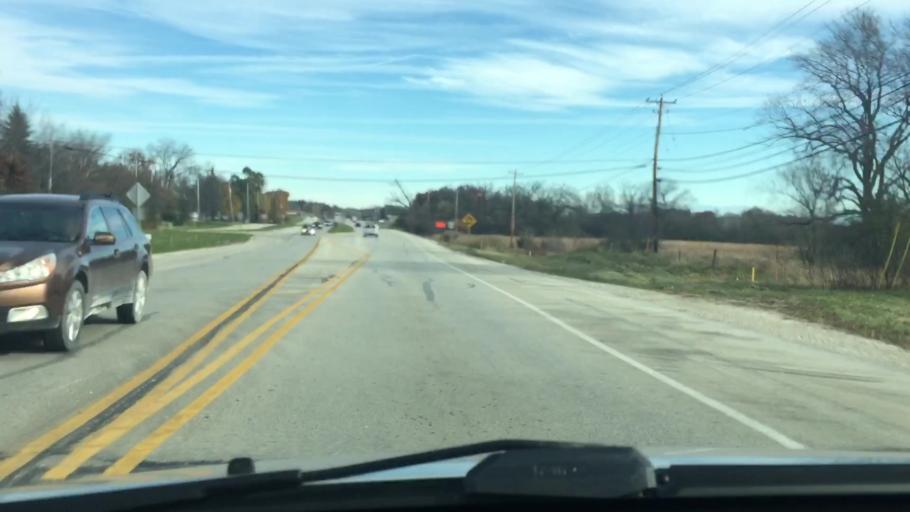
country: US
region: Wisconsin
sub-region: Waukesha County
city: Waukesha
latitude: 42.9823
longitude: -88.2723
